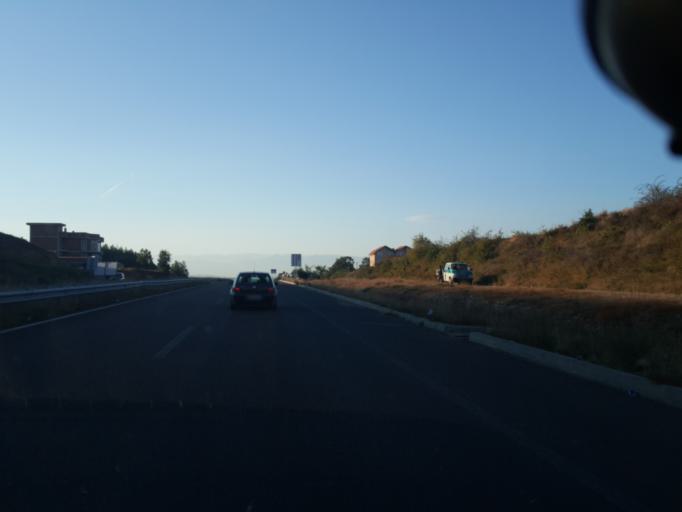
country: XK
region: Prizren
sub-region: Komuna e Malisheves
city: Llazice
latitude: 42.5626
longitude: 20.7730
